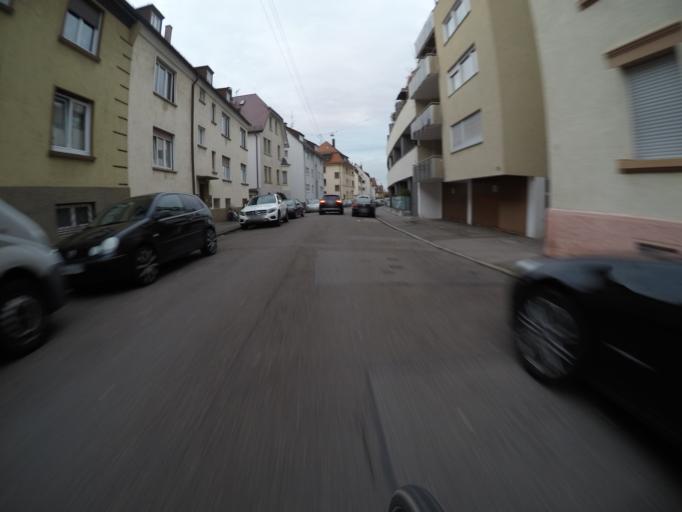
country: DE
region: Baden-Wuerttemberg
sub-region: Regierungsbezirk Stuttgart
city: Stuttgart-Ost
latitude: 48.7735
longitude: 9.2388
